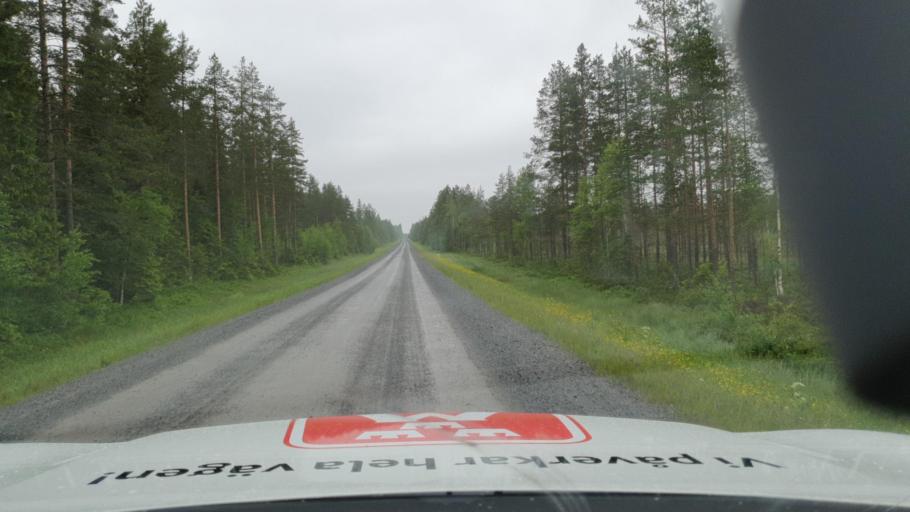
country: SE
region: Vaesterbotten
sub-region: Nordmalings Kommun
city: Nordmaling
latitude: 63.8209
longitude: 19.4942
